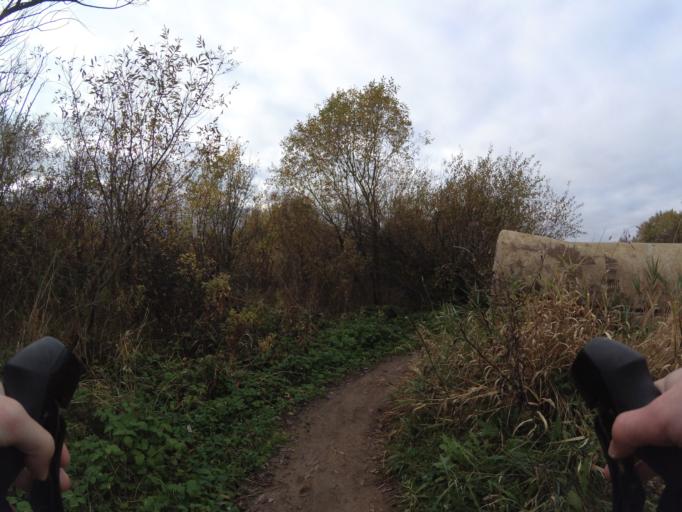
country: RU
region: St.-Petersburg
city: Lakhtinskiy
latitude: 60.0053
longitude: 30.1494
